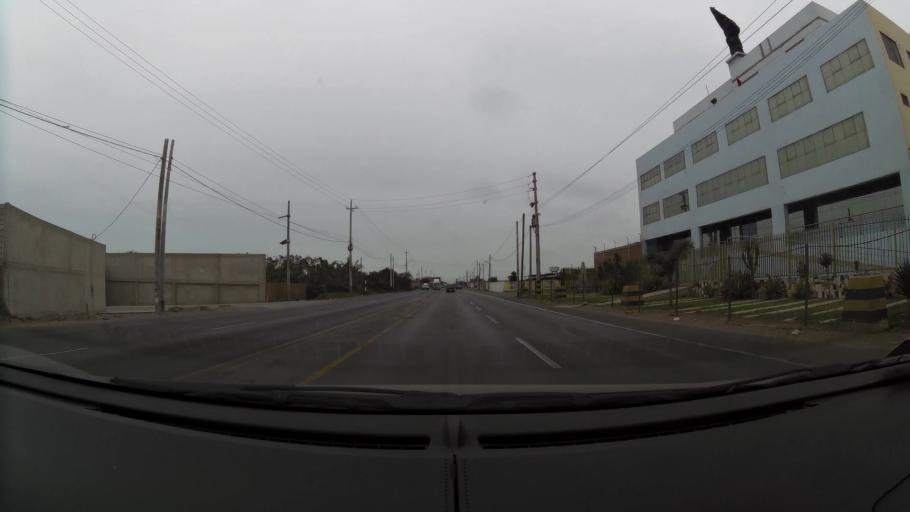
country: PE
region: La Libertad
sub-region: Provincia de Trujillo
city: Moche
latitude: -8.1729
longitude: -78.9996
